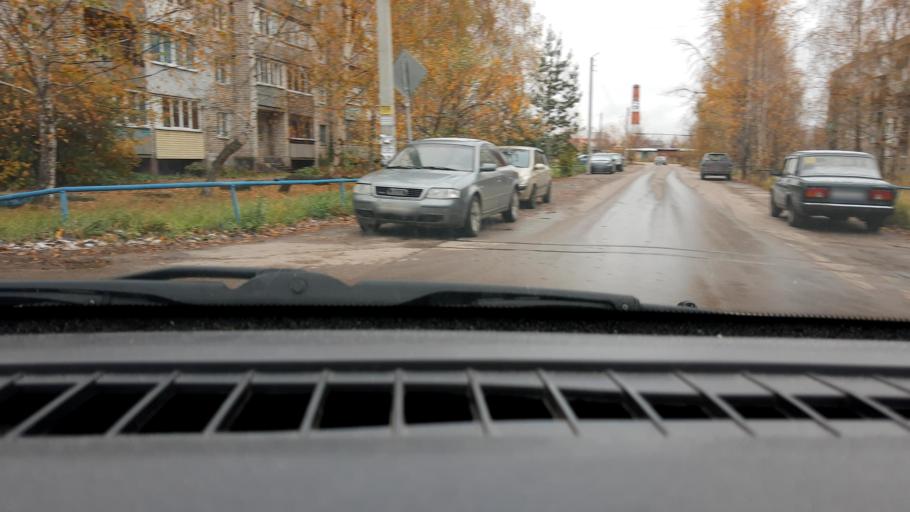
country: RU
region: Nizjnij Novgorod
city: Afonino
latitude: 56.2119
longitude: 44.0991
